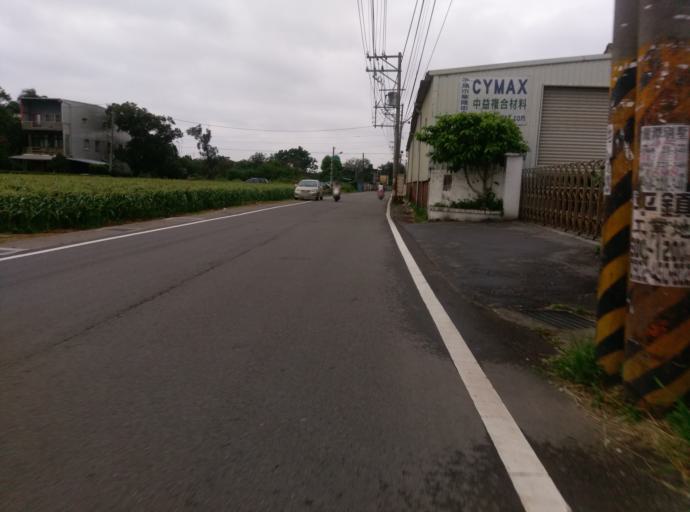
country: TW
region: Taiwan
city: Daxi
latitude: 24.9135
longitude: 121.2387
